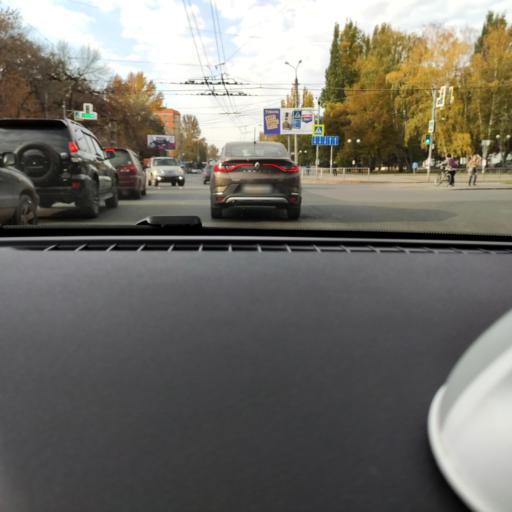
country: RU
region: Samara
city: Samara
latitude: 53.2351
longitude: 50.2208
